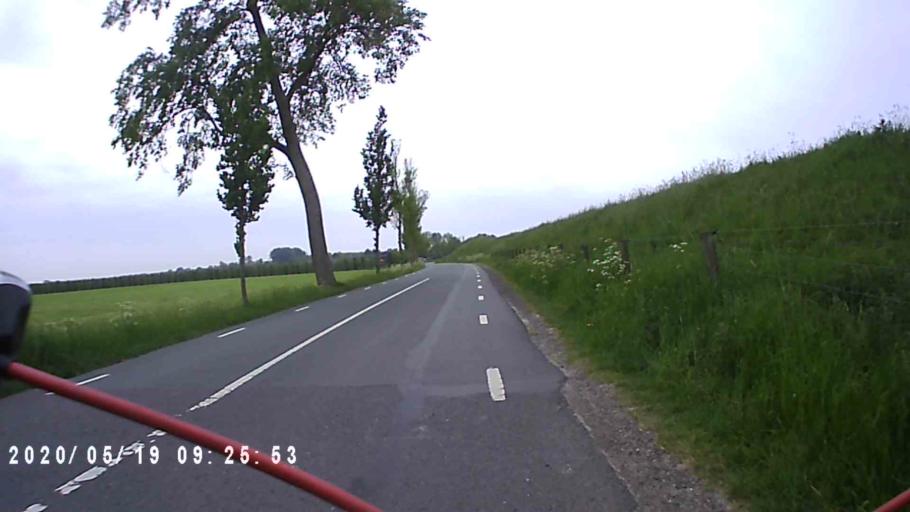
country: NL
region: Groningen
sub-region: Gemeente Zuidhorn
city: Grijpskerk
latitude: 53.2899
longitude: 6.3335
